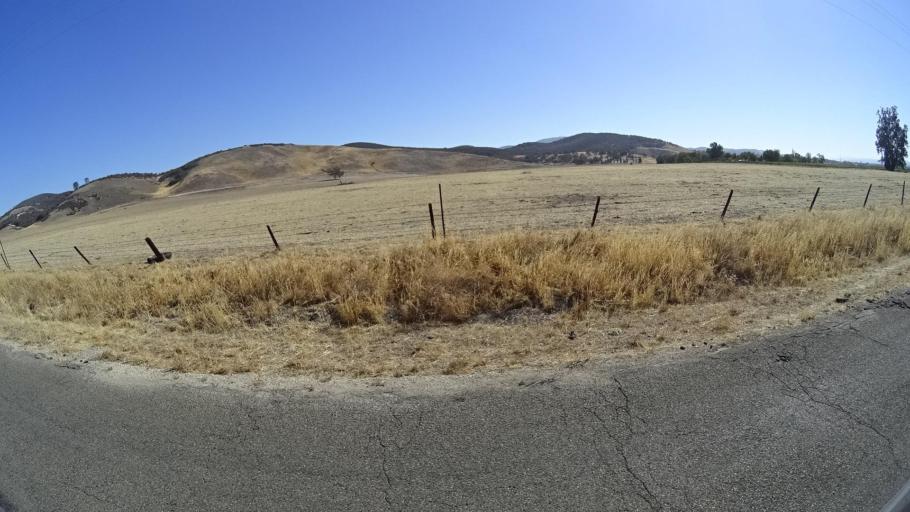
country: US
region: California
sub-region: Monterey County
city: King City
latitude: 35.9693
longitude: -121.0871
